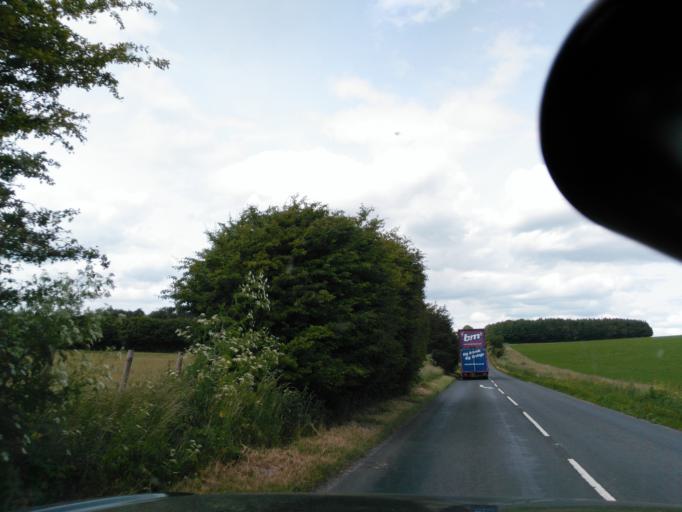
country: GB
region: England
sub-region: Wiltshire
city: Woodford
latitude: 51.1457
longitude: -1.8589
